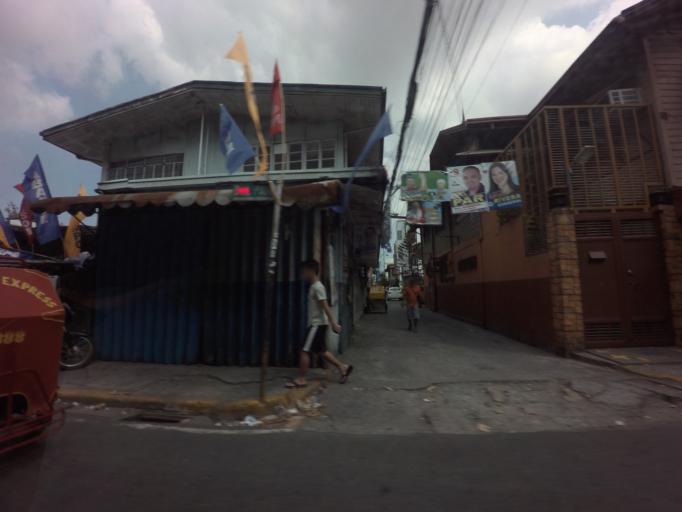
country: PH
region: Metro Manila
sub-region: Mandaluyong
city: Mandaluyong City
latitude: 14.5757
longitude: 121.0127
